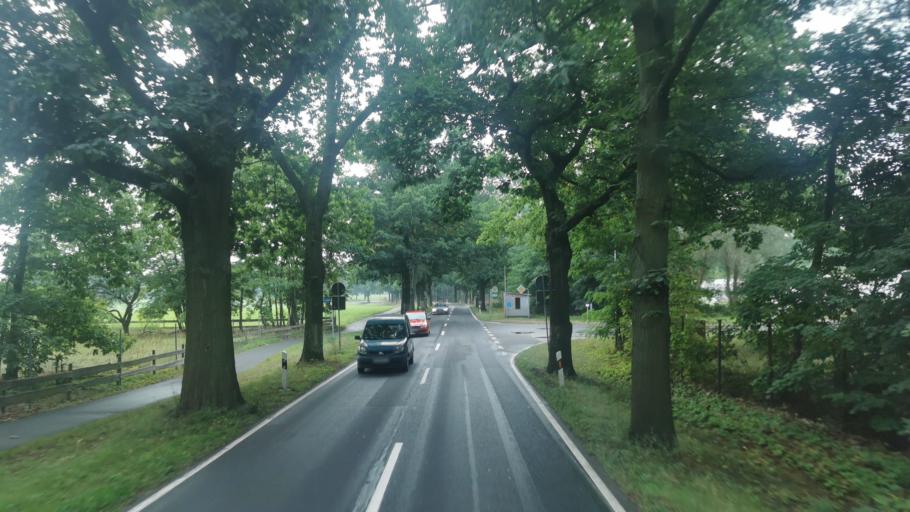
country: DE
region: Brandenburg
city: Kolkwitz
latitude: 51.7348
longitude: 14.2601
